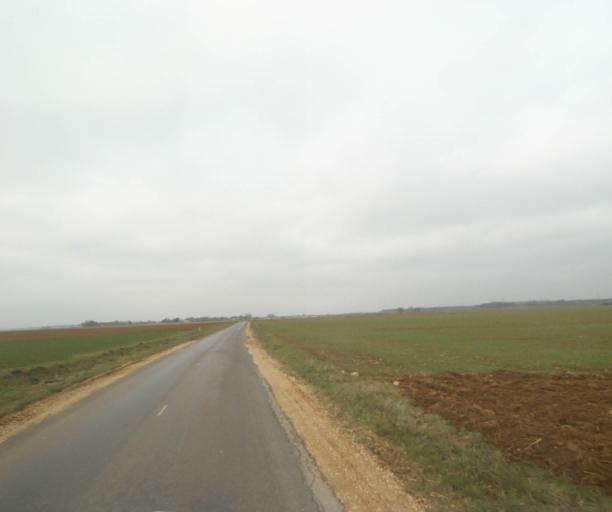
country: FR
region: Champagne-Ardenne
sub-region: Departement de la Haute-Marne
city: Villiers-en-Lieu
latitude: 48.6776
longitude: 4.8549
